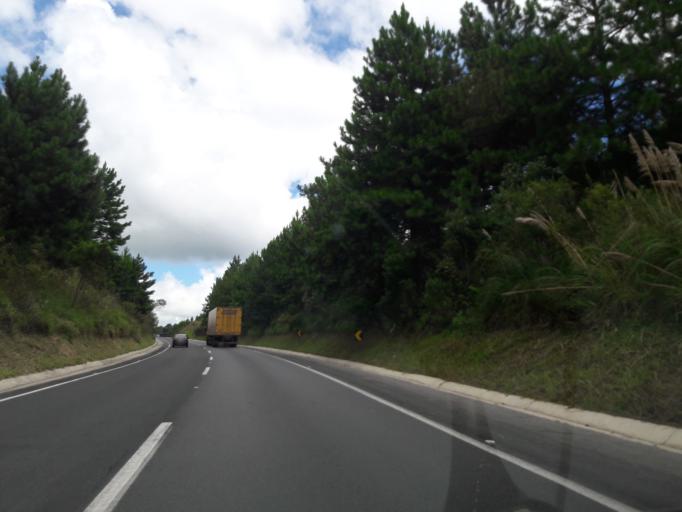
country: BR
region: Parana
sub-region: Campina Grande Do Sul
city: Campina Grande do Sul
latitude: -25.1068
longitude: -48.8493
